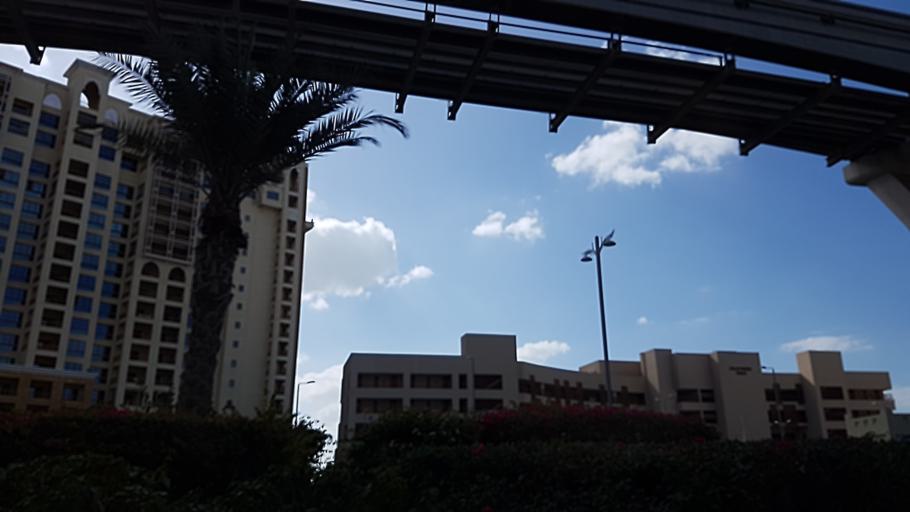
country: AE
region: Dubai
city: Dubai
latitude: 25.1159
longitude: 55.1365
